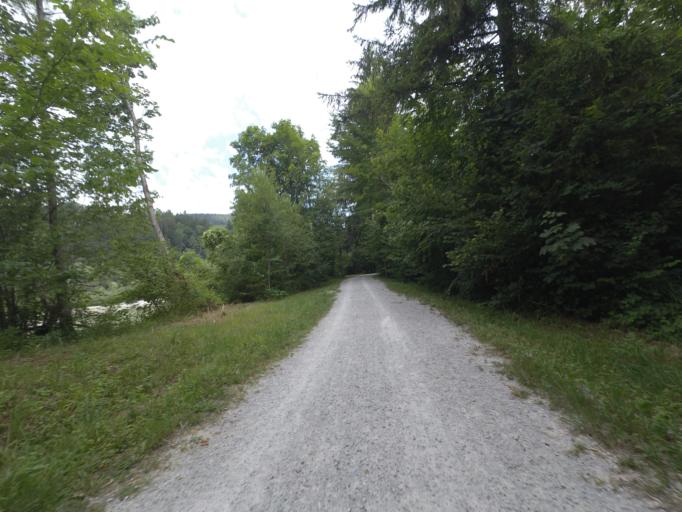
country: DE
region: Bavaria
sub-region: Upper Bavaria
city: Piding
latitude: 47.7823
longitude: 12.9398
